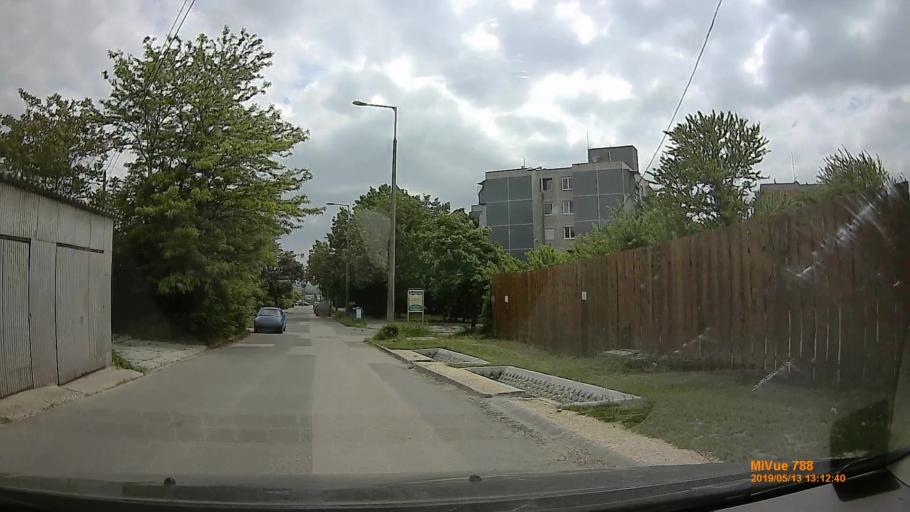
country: HU
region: Budapest
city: Budapest XXII. keruelet
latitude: 47.4108
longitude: 19.0021
